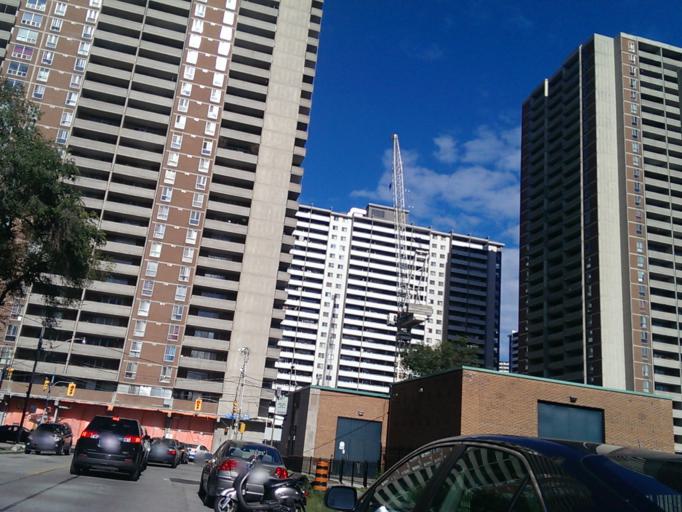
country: CA
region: Ontario
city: Toronto
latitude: 43.6694
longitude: -79.3765
